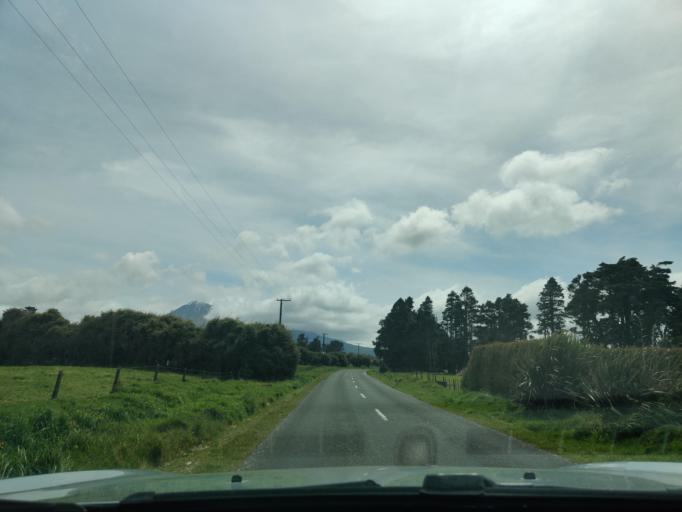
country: NZ
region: Taranaki
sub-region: South Taranaki District
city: Eltham
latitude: -39.3783
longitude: 174.1454
